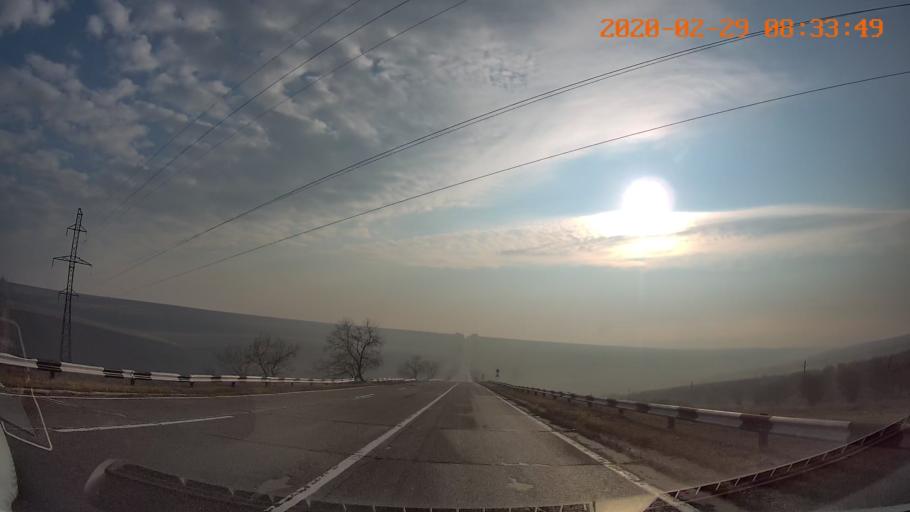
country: MD
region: Anenii Noi
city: Anenii Noi
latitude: 46.9265
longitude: 29.2977
